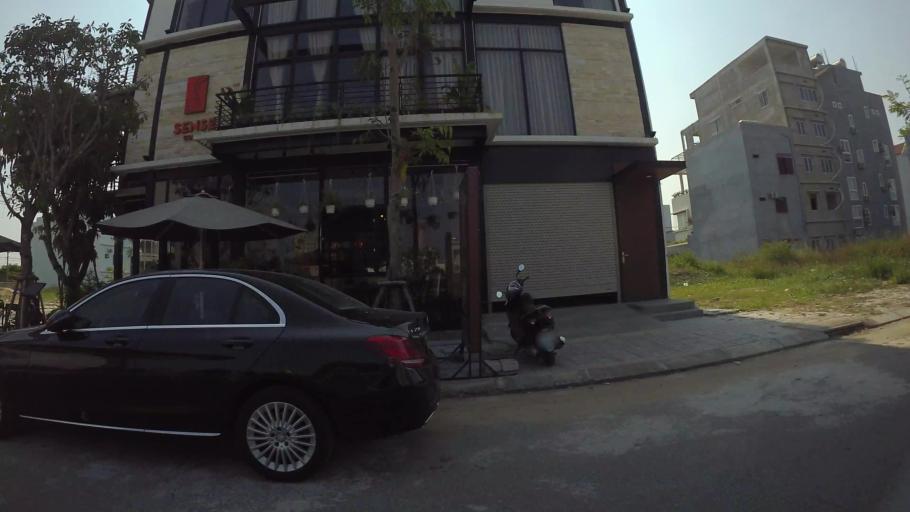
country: VN
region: Da Nang
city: Ngu Hanh Son
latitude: 16.0374
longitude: 108.2470
